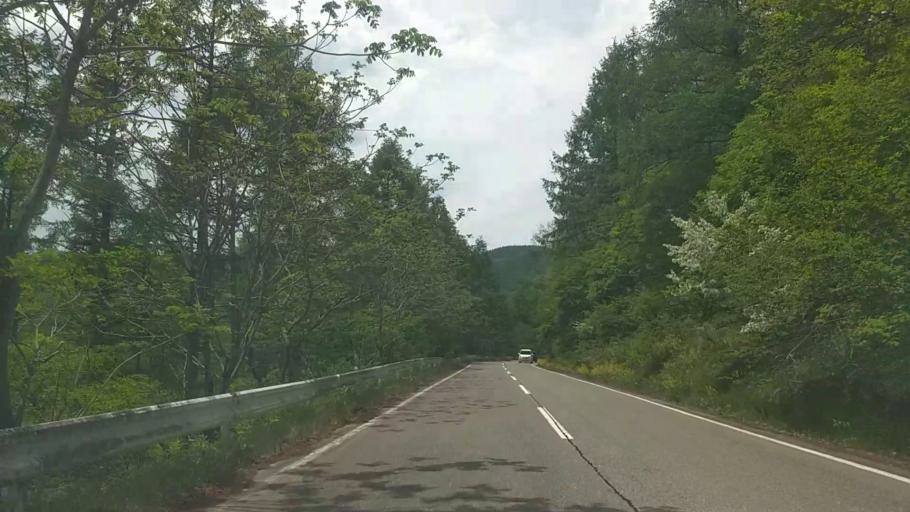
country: JP
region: Nagano
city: Saku
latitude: 36.1025
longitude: 138.3953
